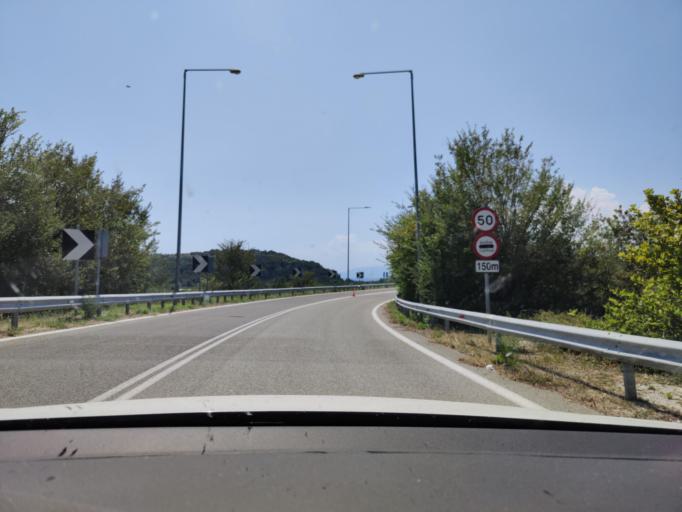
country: GR
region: East Macedonia and Thrace
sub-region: Nomos Kavalas
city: Paralia Ofryniou
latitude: 40.7838
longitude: 23.9589
